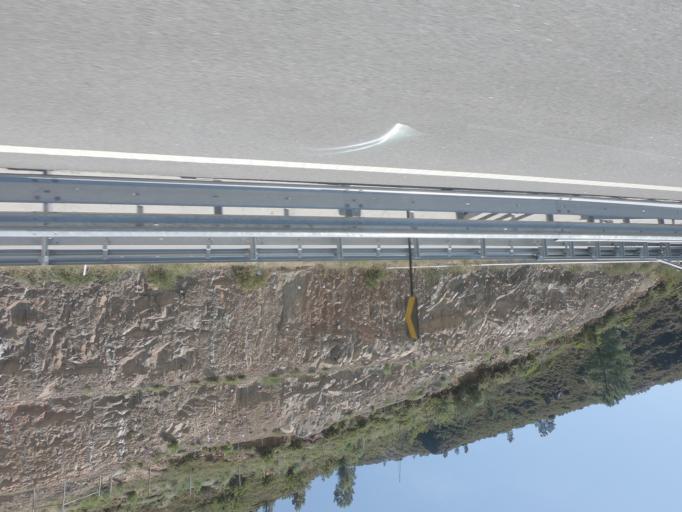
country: PT
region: Porto
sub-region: Baiao
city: Valadares
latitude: 41.2580
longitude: -7.9469
